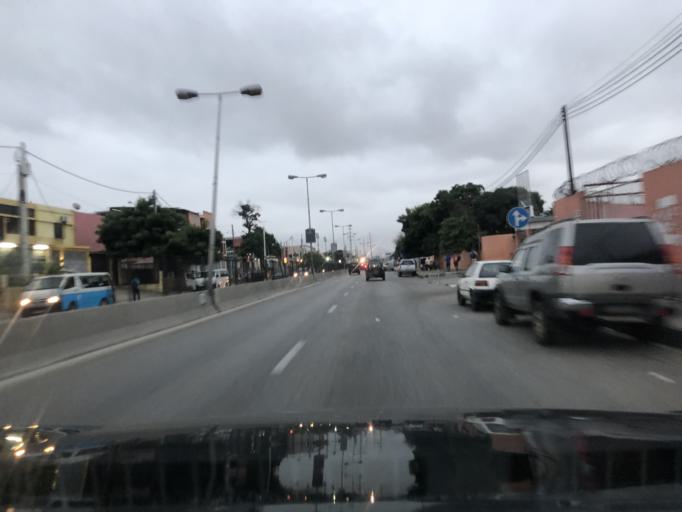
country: AO
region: Luanda
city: Luanda
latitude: -8.8448
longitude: 13.2364
